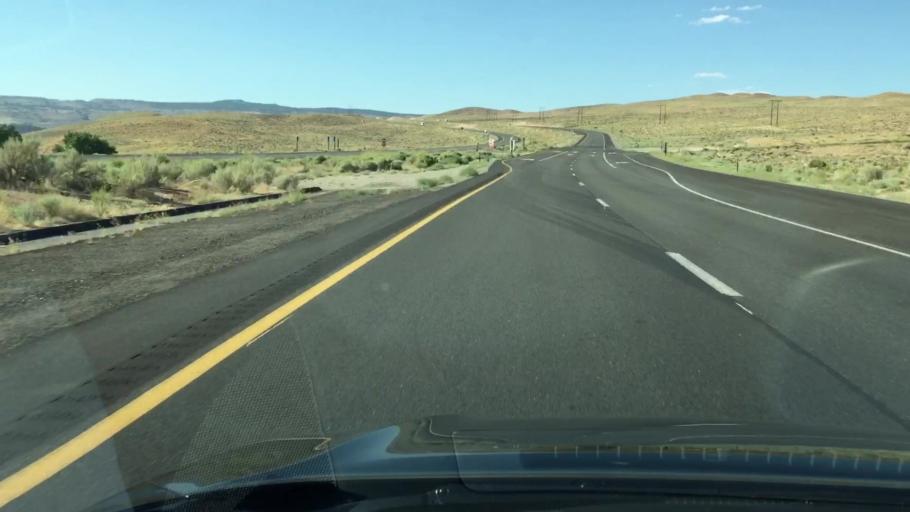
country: US
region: California
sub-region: Inyo County
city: West Bishop
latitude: 37.4448
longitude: -118.5745
